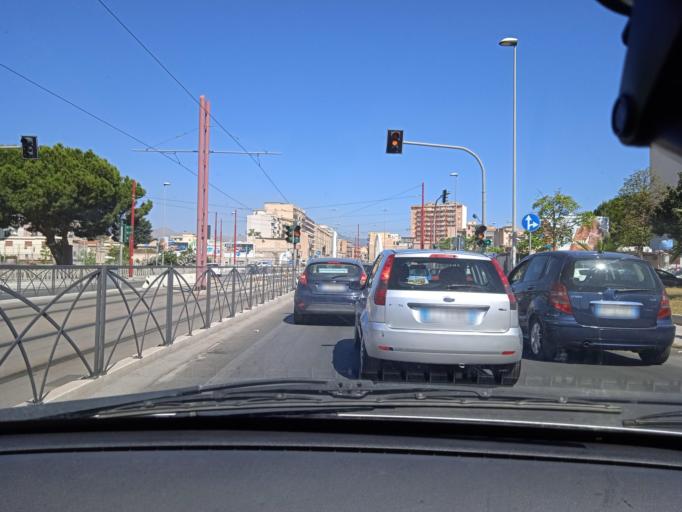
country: IT
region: Sicily
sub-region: Palermo
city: Ciaculli
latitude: 38.1053
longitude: 13.3757
